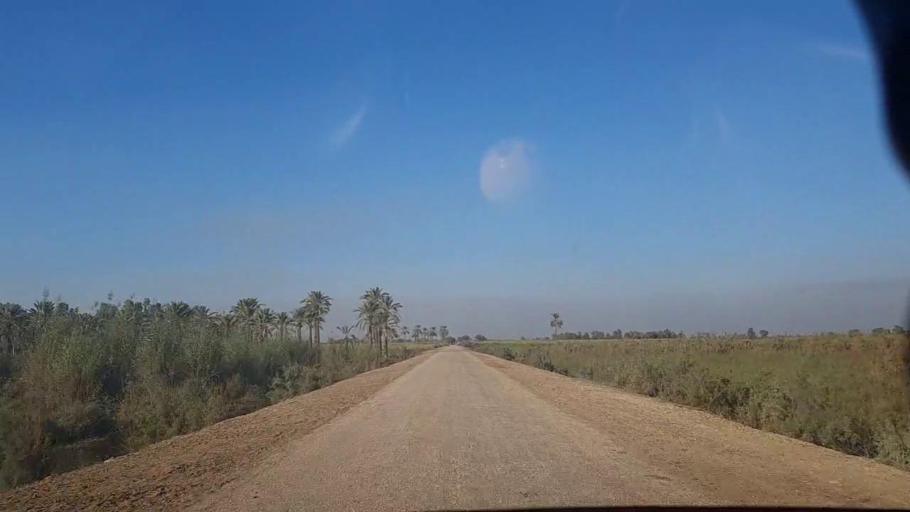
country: PK
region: Sindh
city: Sobhadero
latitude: 27.4071
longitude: 68.4221
